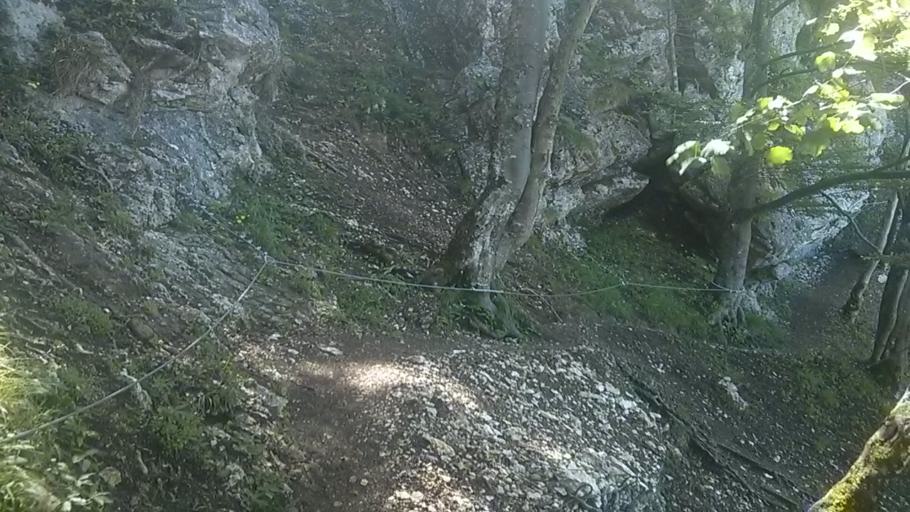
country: FR
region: Rhone-Alpes
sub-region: Departement de la Savoie
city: Le Bourget-du-Lac
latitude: 45.6759
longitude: 5.8338
